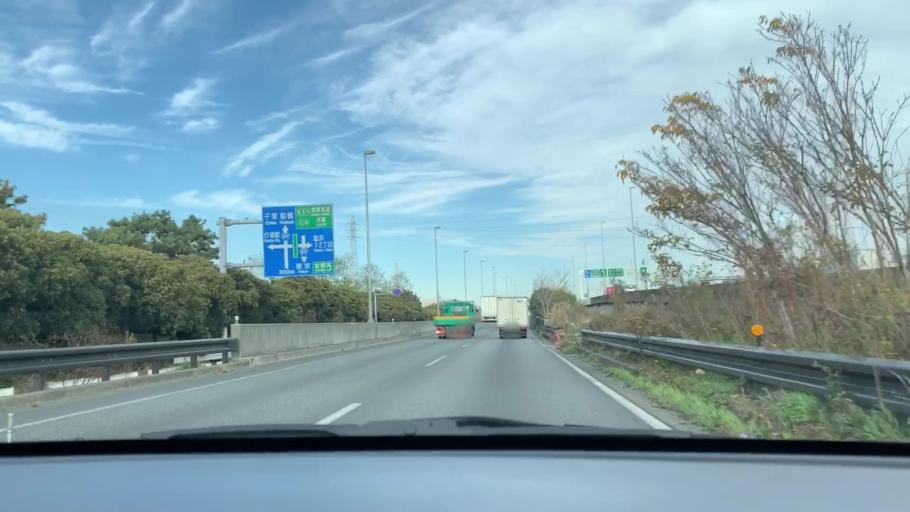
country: JP
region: Tokyo
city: Urayasu
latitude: 35.6697
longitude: 139.9238
